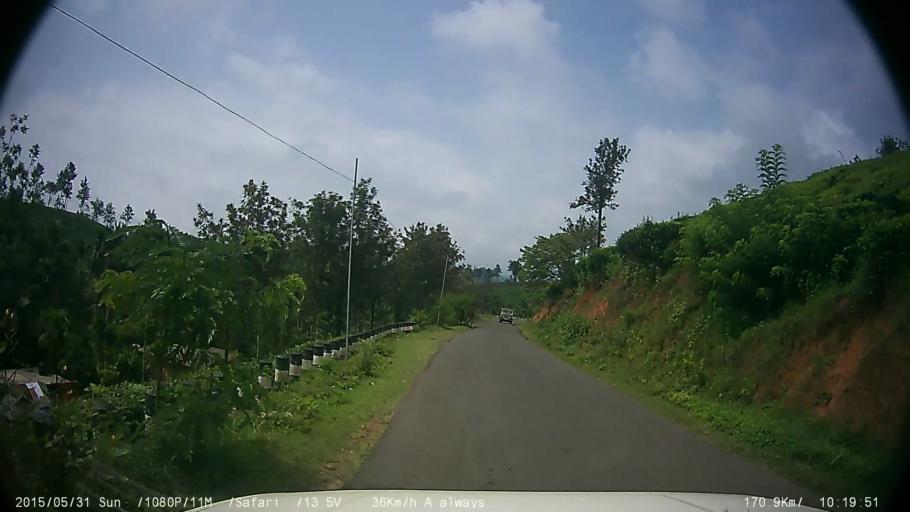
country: IN
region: Kerala
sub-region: Wayanad
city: Kalpetta
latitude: 11.5480
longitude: 76.1386
